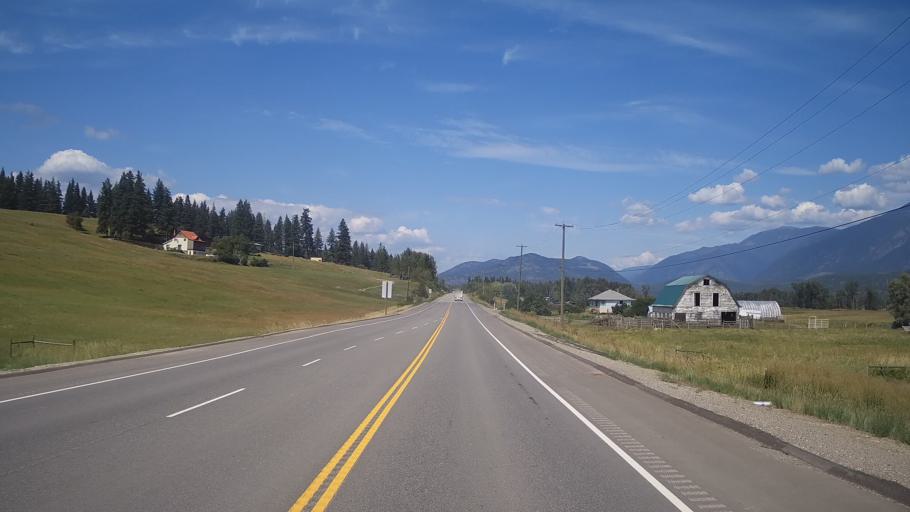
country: CA
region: British Columbia
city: Kamloops
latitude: 51.3018
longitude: -120.1818
